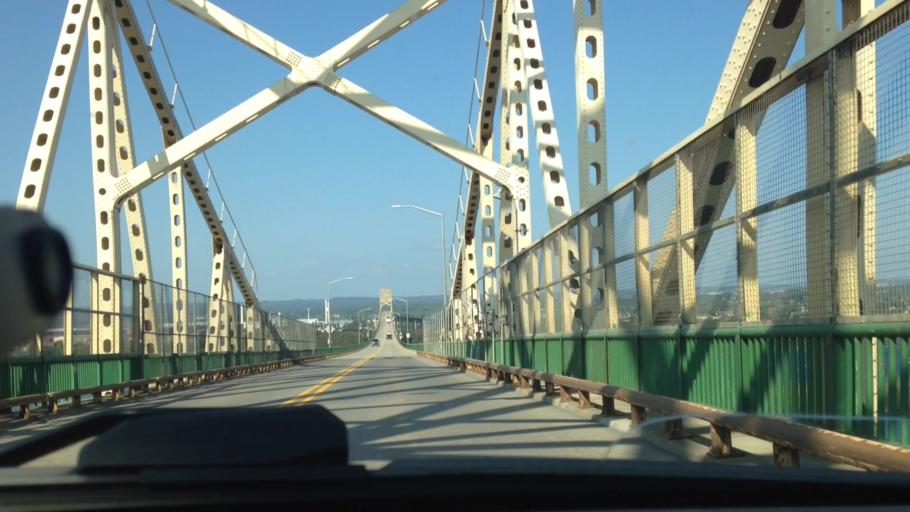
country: US
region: Michigan
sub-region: Chippewa County
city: Sault Ste. Marie
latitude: 46.5039
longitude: -84.3626
